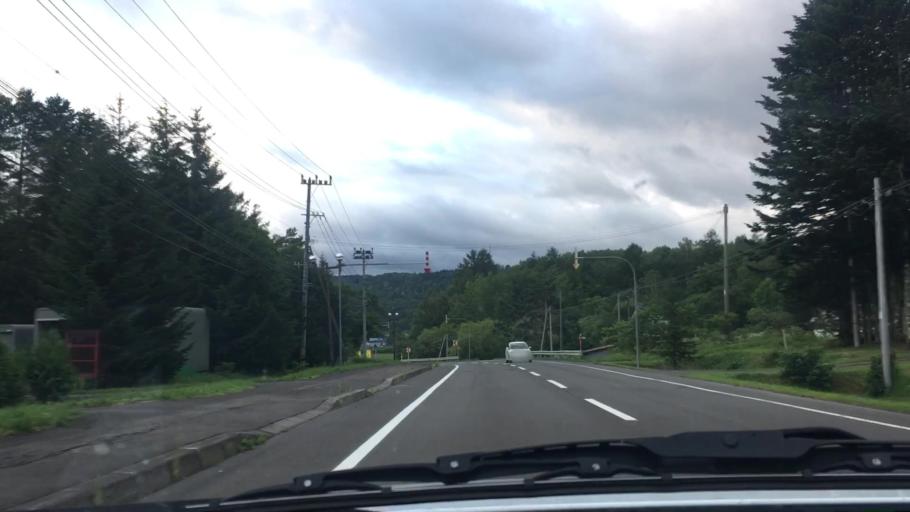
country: JP
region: Hokkaido
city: Shimo-furano
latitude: 42.9885
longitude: 142.3989
